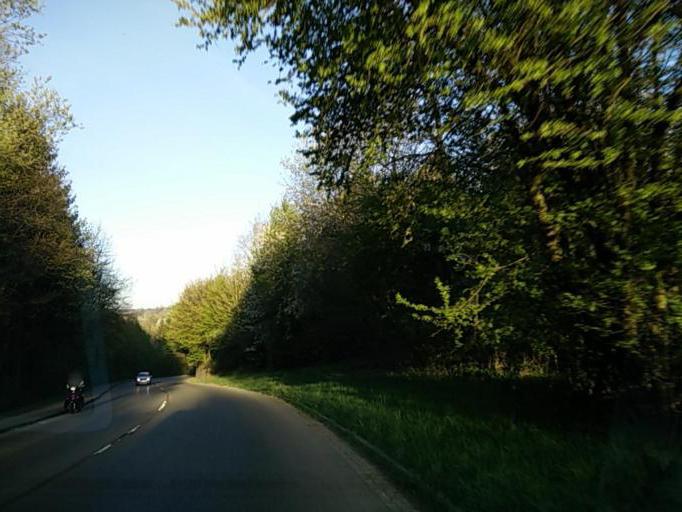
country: DE
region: Baden-Wuerttemberg
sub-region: Tuebingen Region
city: Tuebingen
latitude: 48.5386
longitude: 9.0255
